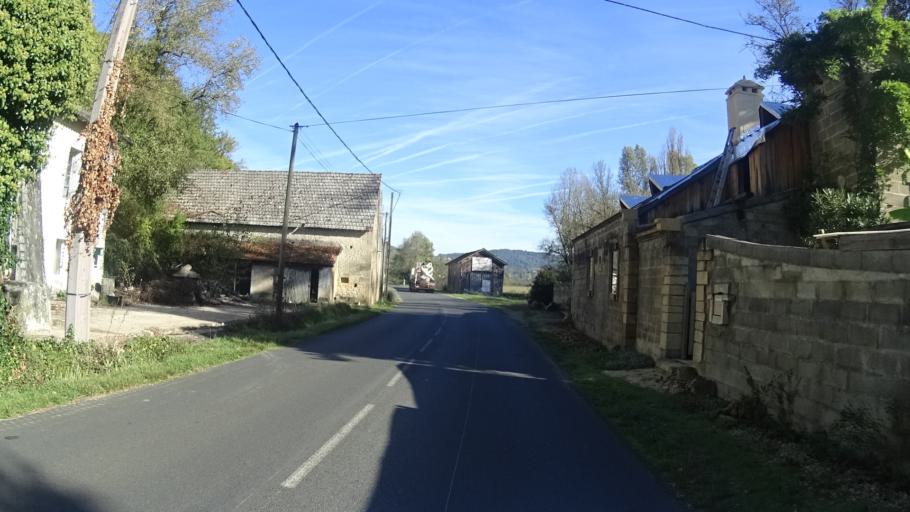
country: FR
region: Aquitaine
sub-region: Departement de la Dordogne
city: Saint-Cyprien
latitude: 44.8563
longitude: 1.0214
